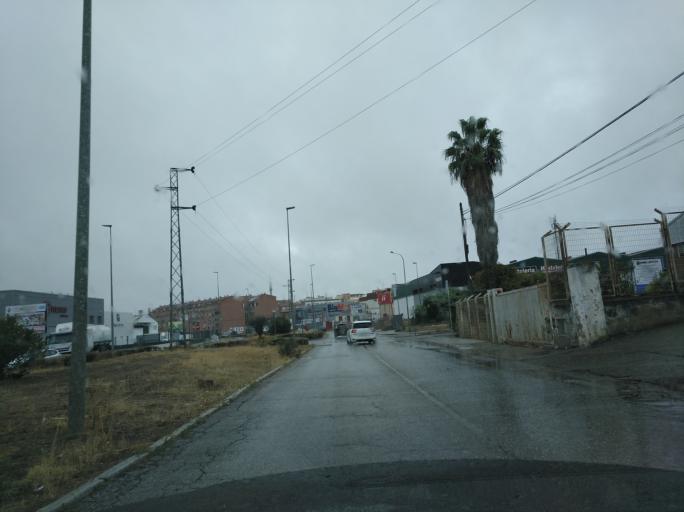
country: ES
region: Extremadura
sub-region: Provincia de Badajoz
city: Badajoz
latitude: 38.8913
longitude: -6.9929
